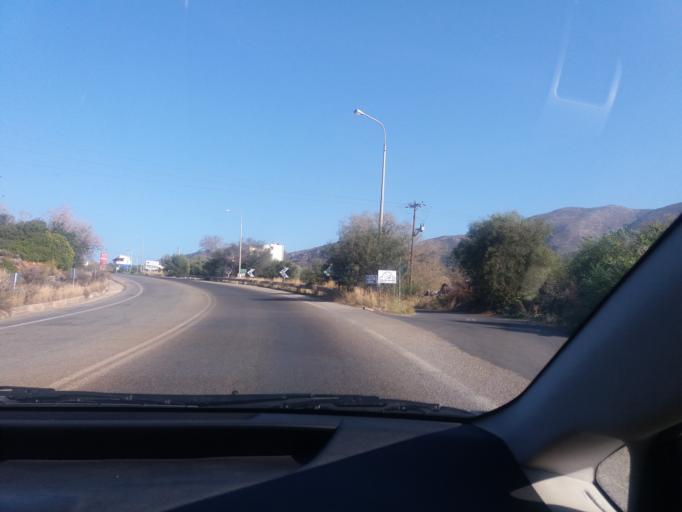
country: GR
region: Crete
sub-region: Nomos Lasithiou
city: Sision
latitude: 35.2908
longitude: 25.5077
